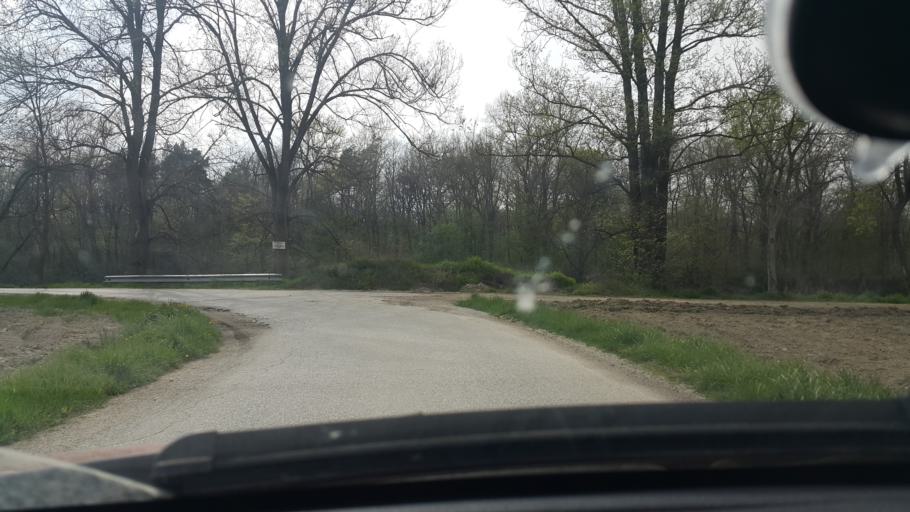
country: SI
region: Duplek
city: Zgornji Duplek
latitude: 46.5336
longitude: 15.7195
